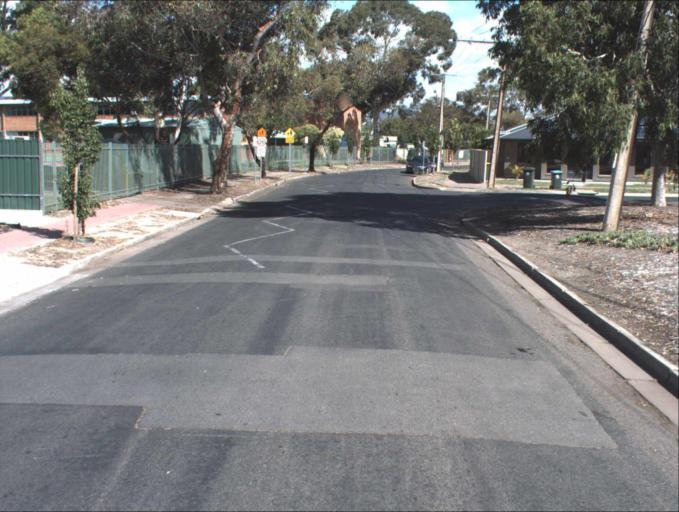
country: AU
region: South Australia
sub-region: Port Adelaide Enfield
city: Gilles Plains
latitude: -34.8578
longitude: 138.6506
